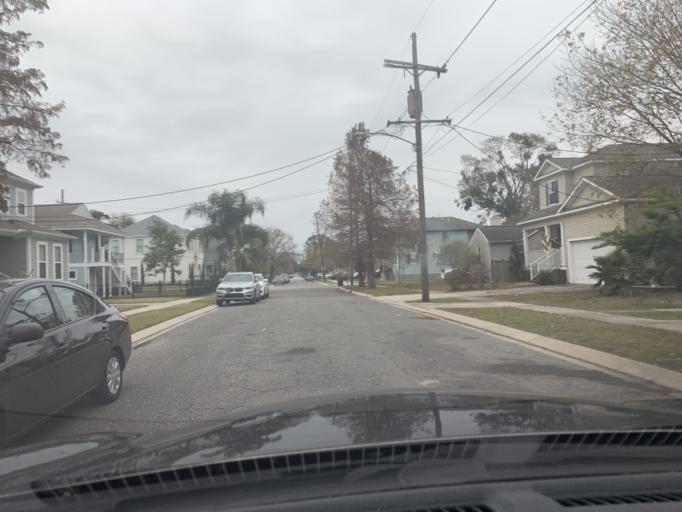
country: US
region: Louisiana
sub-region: Jefferson Parish
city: Metairie
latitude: 29.9981
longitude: -90.1141
